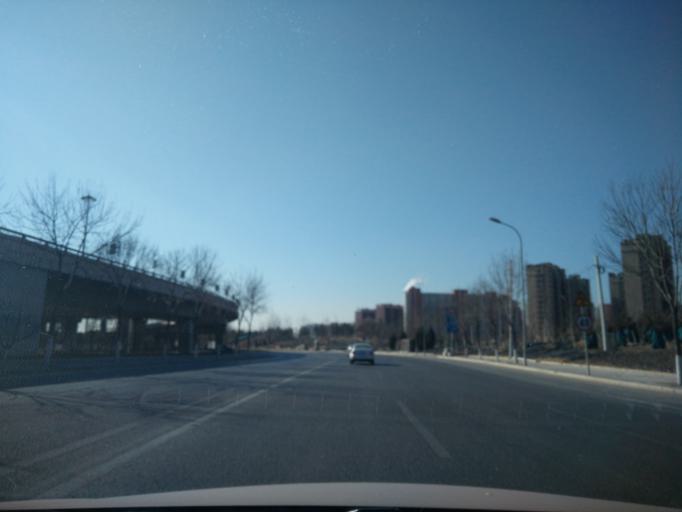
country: CN
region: Beijing
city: Yinghai
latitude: 39.7852
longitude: 116.4232
